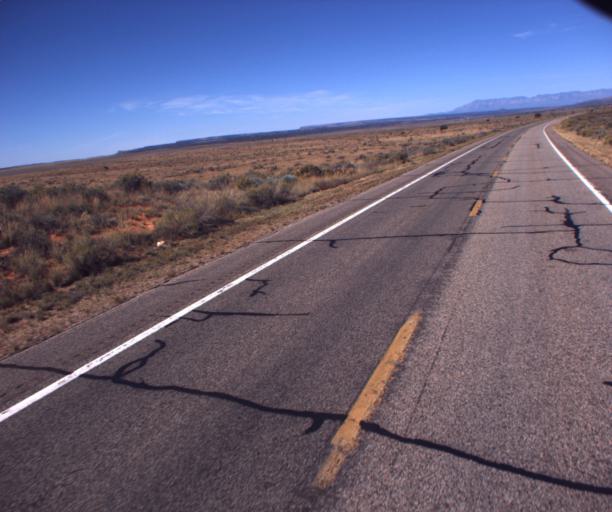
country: US
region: Arizona
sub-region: Mohave County
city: Colorado City
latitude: 36.8888
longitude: -112.9090
